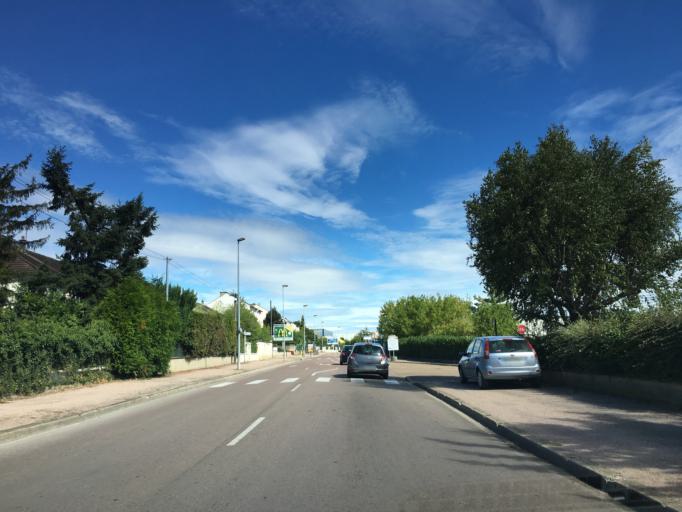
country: FR
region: Bourgogne
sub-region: Departement de l'Yonne
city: Auxerre
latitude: 47.8014
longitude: 3.5530
